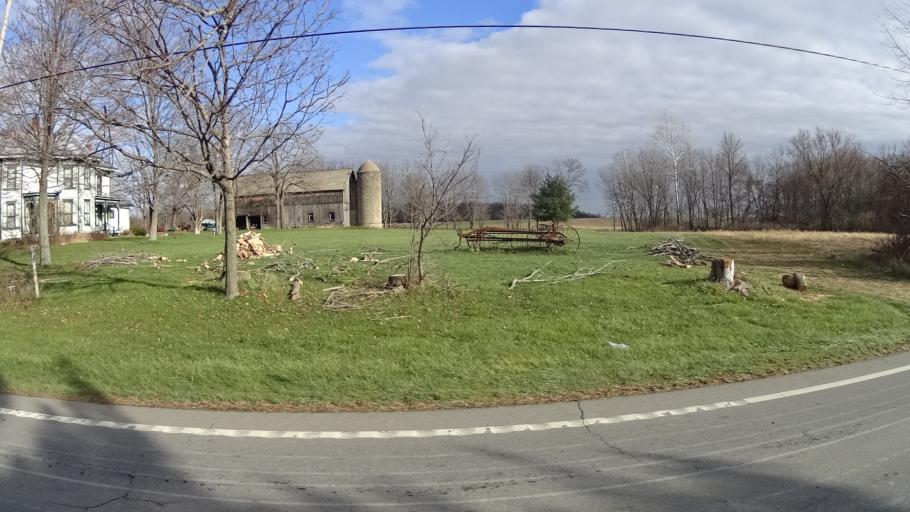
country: US
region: Ohio
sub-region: Lorain County
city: Wellington
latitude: 41.1364
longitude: -82.3076
